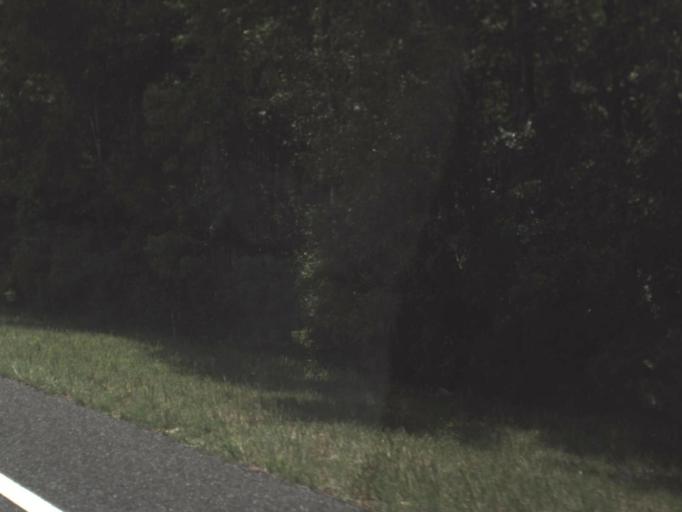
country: US
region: Florida
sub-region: Taylor County
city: Steinhatchee
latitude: 29.6864
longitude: -83.2676
